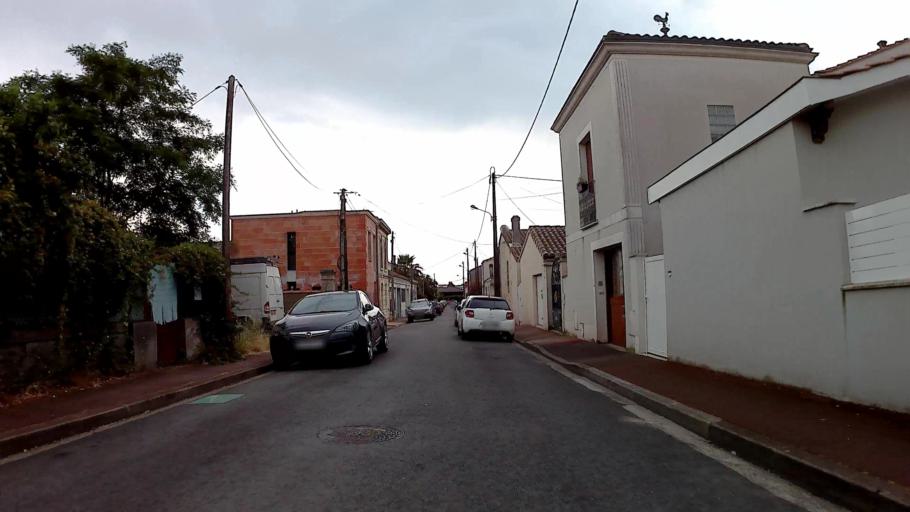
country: FR
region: Aquitaine
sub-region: Departement de la Gironde
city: Le Bouscat
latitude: 44.8660
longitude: -0.5904
